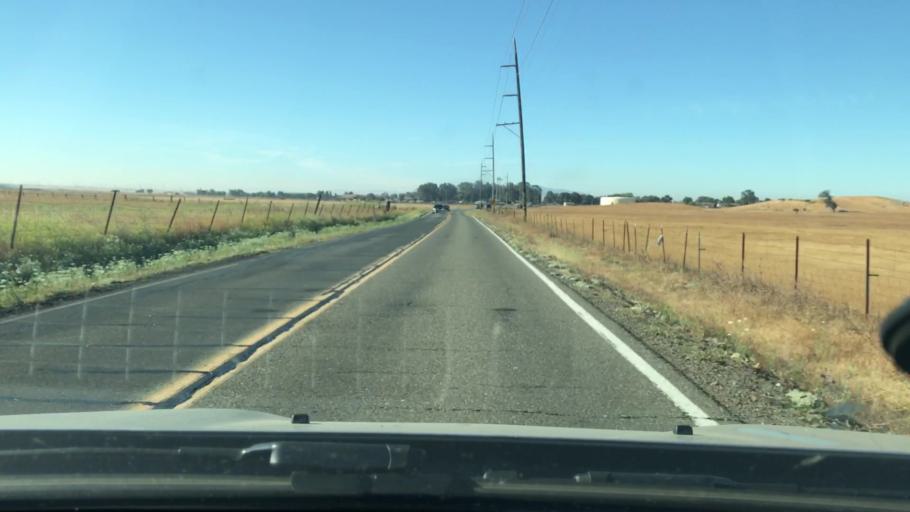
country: US
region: California
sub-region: Solano County
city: Vacaville
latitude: 38.2952
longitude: -121.9333
